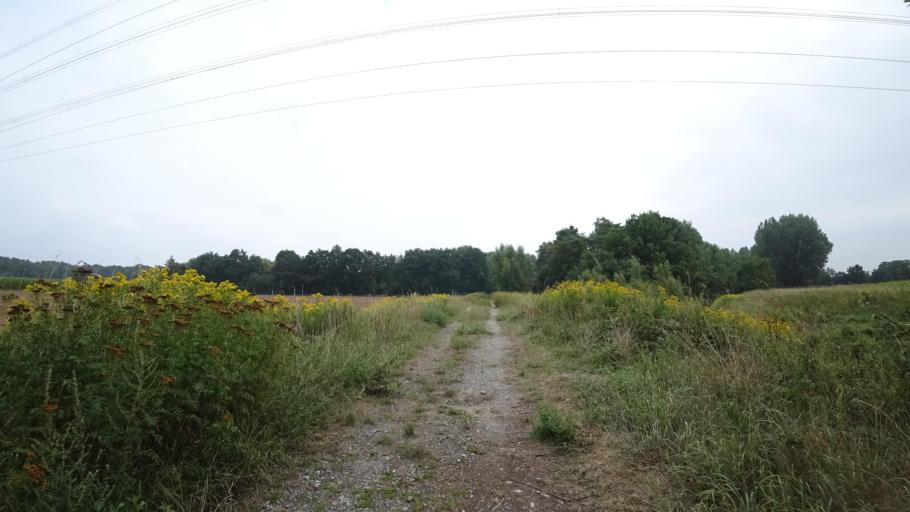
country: DE
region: North Rhine-Westphalia
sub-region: Regierungsbezirk Detmold
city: Guetersloh
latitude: 51.9046
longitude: 8.3240
